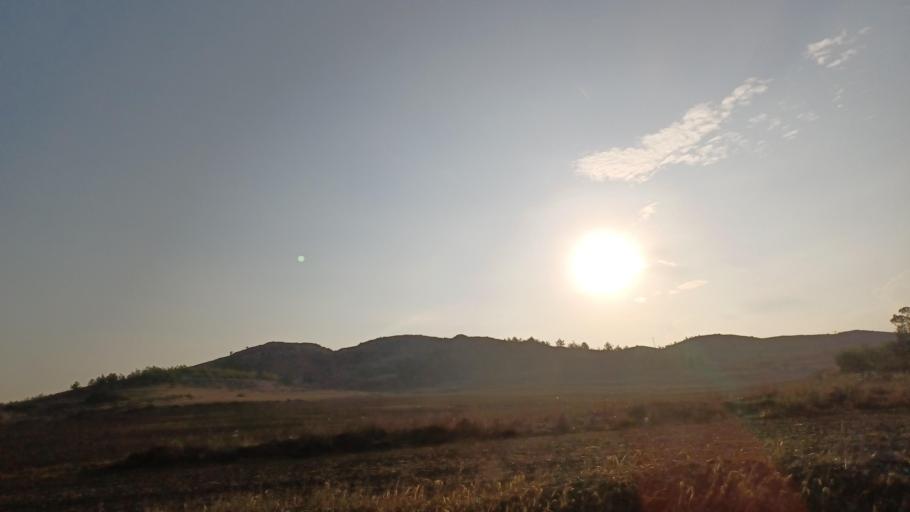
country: CY
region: Larnaka
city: Athienou
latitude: 35.0478
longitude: 33.4998
